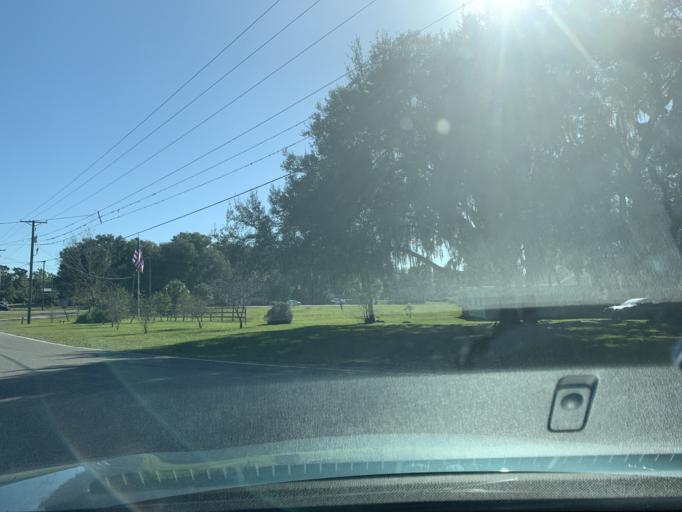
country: US
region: Florida
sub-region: Pasco County
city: San Antonio
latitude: 28.3356
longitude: -82.2716
